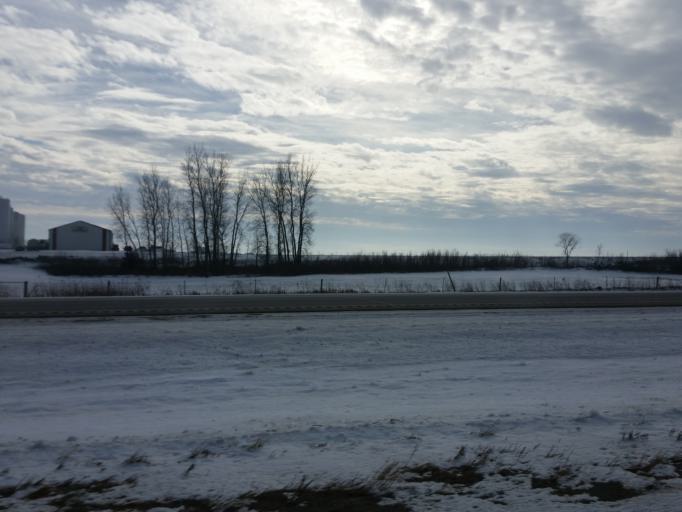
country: US
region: Iowa
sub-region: Buchanan County
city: Independence
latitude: 42.4484
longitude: -91.9141
